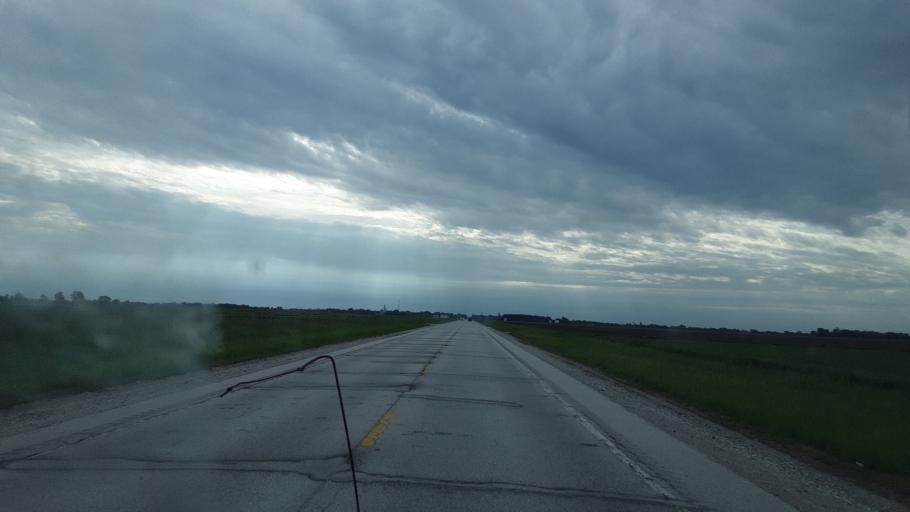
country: US
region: Illinois
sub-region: Hancock County
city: Hamilton
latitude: 40.3954
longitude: -91.2836
